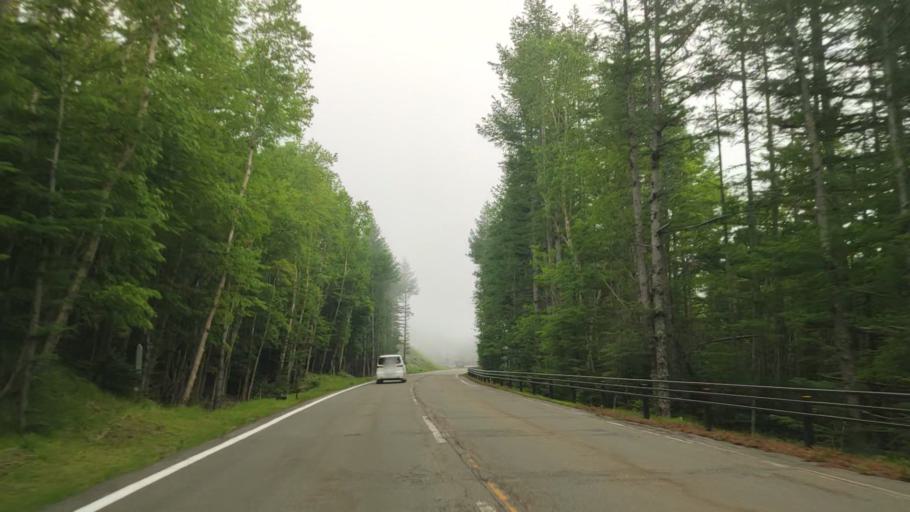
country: JP
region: Yamanashi
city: Fujikawaguchiko
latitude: 35.3758
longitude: 138.6920
